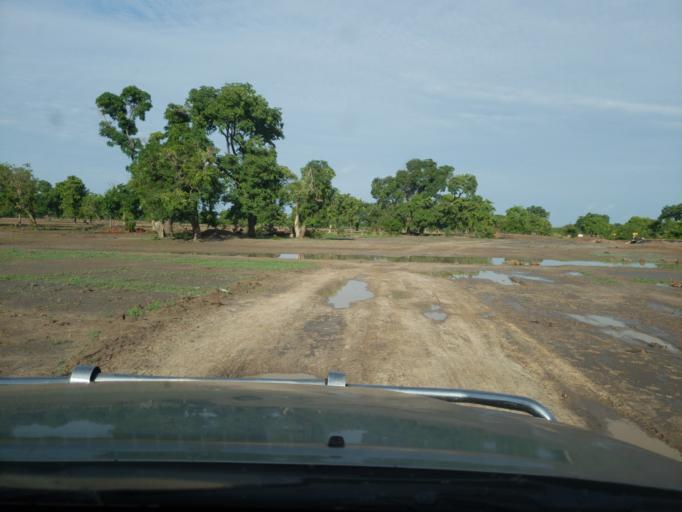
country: ML
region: Sikasso
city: Koutiala
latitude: 12.4187
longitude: -5.7034
